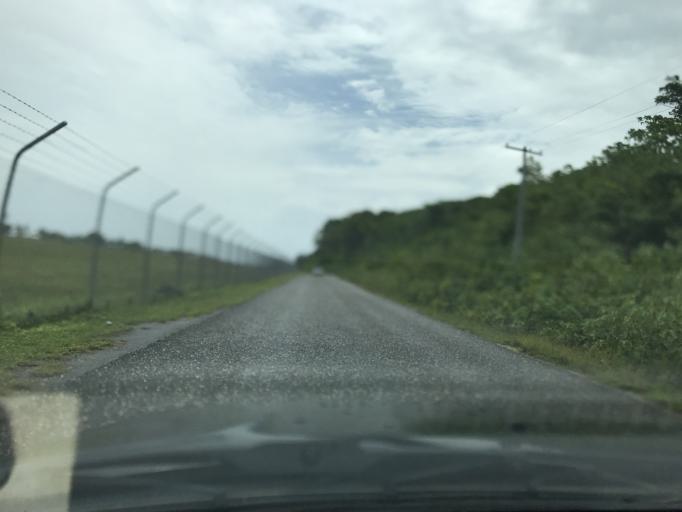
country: SB
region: Western Province
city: Gizo
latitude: -8.3271
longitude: 157.2576
